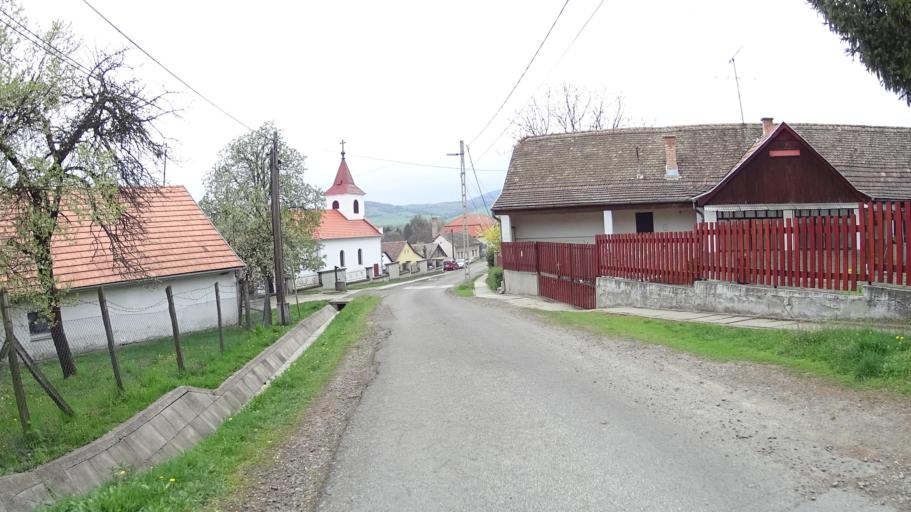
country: HU
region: Pest
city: Kismaros
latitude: 47.8668
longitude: 19.0118
